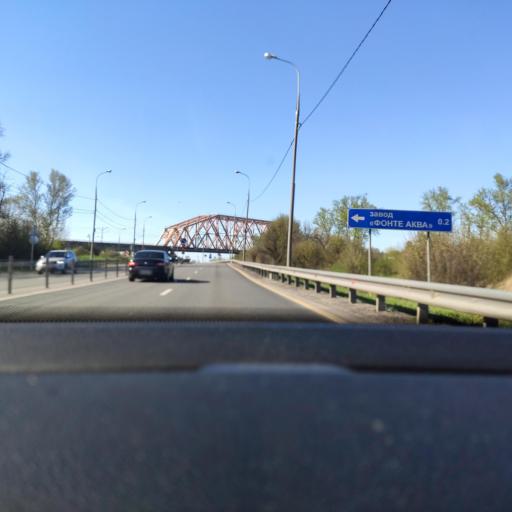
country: RU
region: Moskovskaya
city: Dedenevo
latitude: 56.2562
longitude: 37.5109
